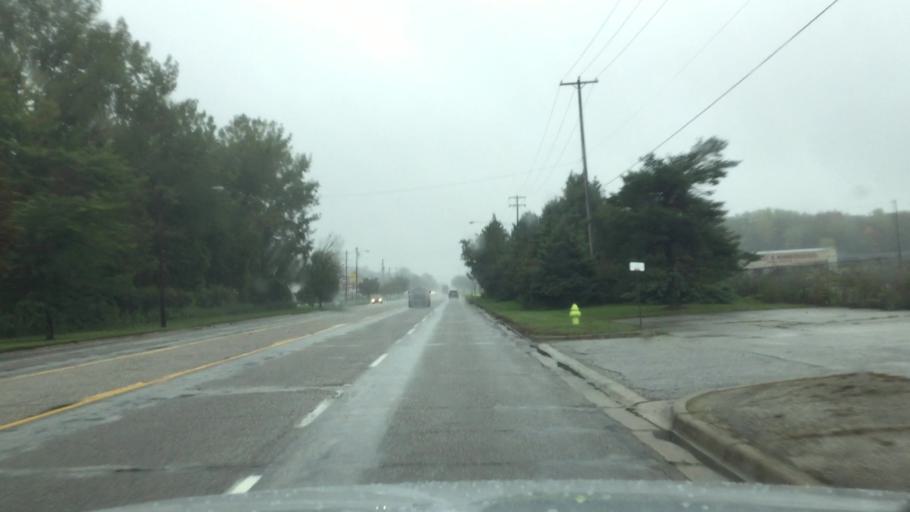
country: US
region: Michigan
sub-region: Saginaw County
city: Bridgeport
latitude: 43.3689
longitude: -83.8883
